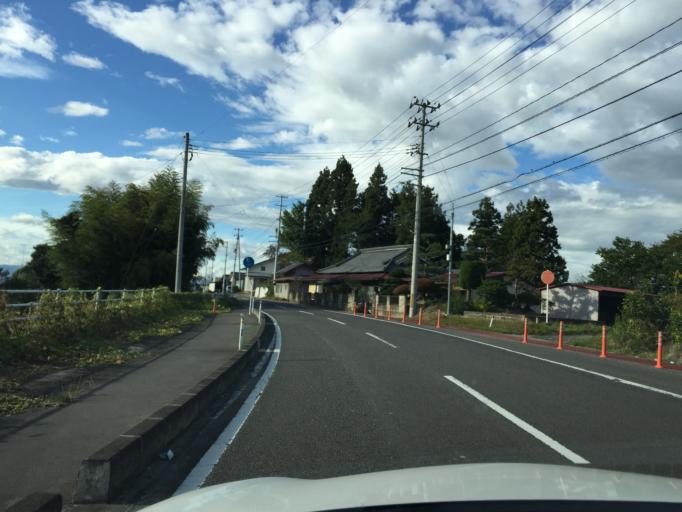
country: JP
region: Fukushima
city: Sukagawa
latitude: 37.2580
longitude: 140.4280
